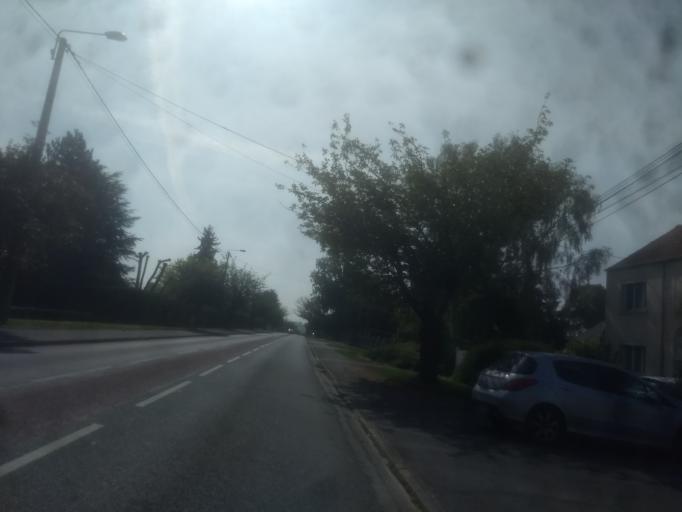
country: FR
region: Nord-Pas-de-Calais
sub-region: Departement du Pas-de-Calais
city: Beaurains
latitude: 50.2598
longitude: 2.7986
